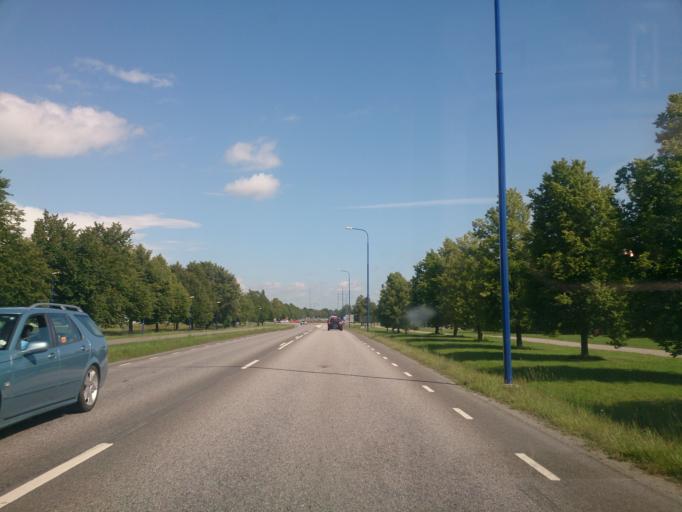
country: SE
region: OEstergoetland
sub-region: Norrkopings Kommun
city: Norrkoping
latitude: 58.6071
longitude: 16.1717
